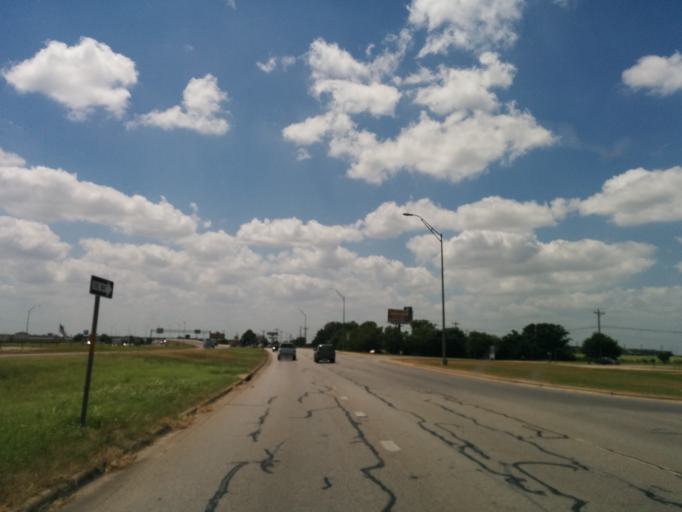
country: US
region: Texas
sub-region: Bastrop County
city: Bastrop
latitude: 30.1104
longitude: -97.3428
